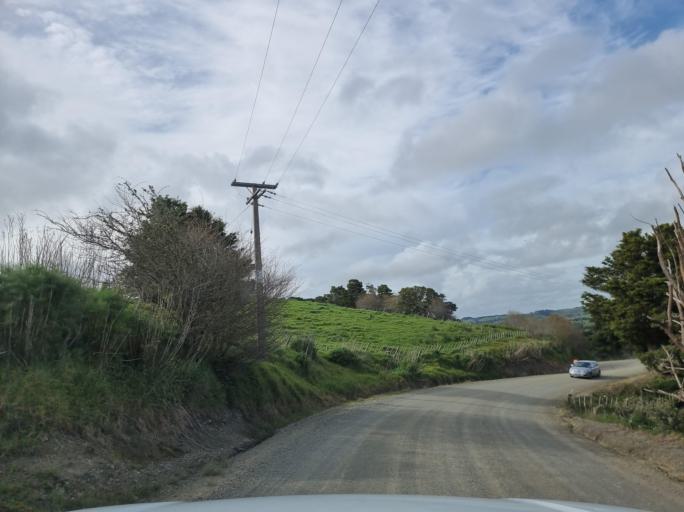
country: NZ
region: Northland
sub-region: Whangarei
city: Ruakaka
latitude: -36.0940
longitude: 174.3664
